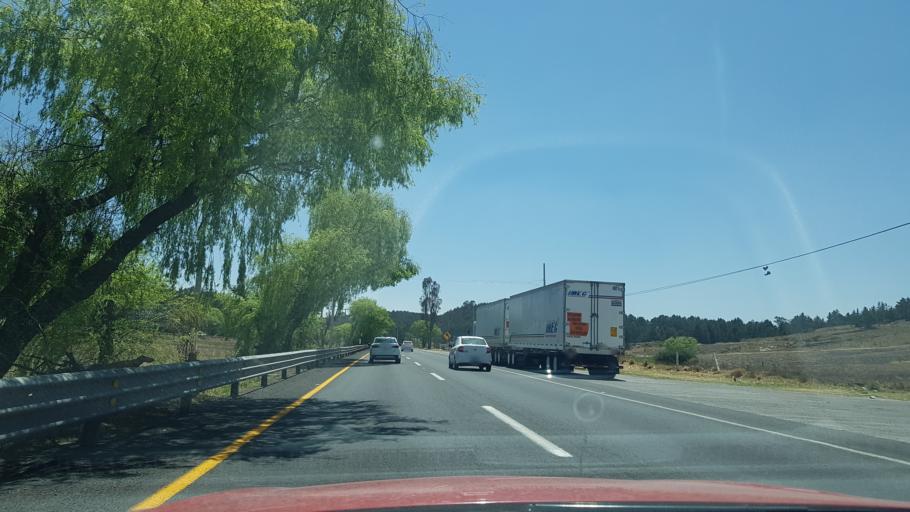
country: MX
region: Mexico
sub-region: Ixtlahuaca
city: San Lorenzo Toxico
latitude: 19.5330
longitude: -99.7467
